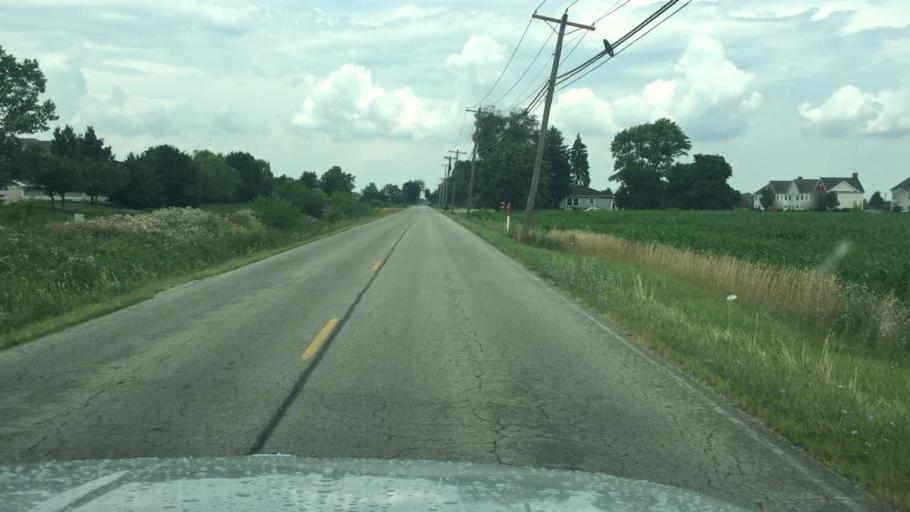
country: US
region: Ohio
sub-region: Wood County
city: Walbridge
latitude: 41.5763
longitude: -83.5277
